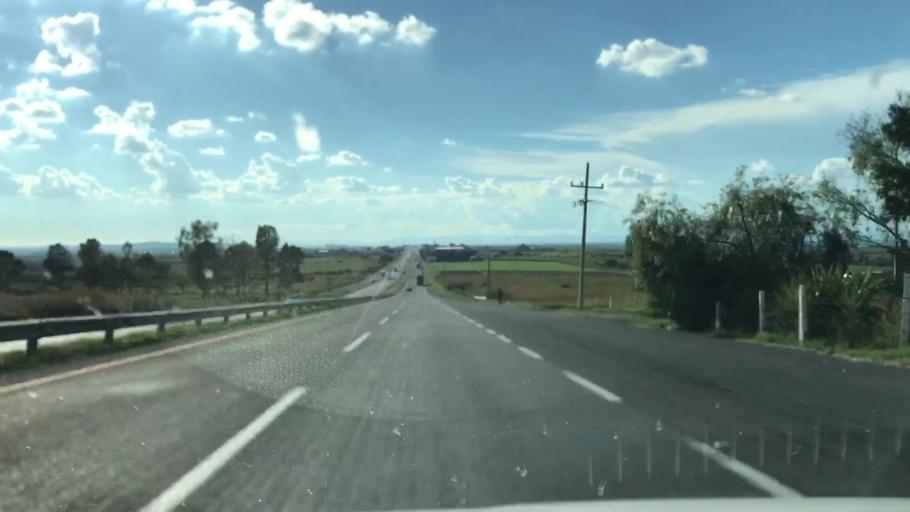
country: MX
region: Jalisco
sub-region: San Juan de los Lagos
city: Mezquitic de la Magdalena
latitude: 21.2897
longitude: -102.2209
